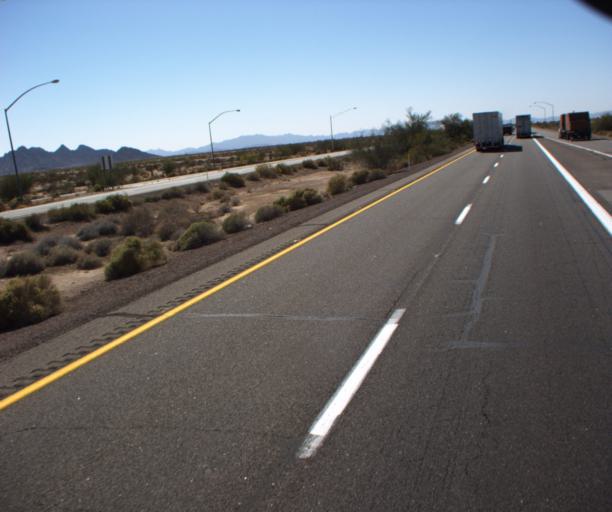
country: US
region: Arizona
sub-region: Yuma County
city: Wellton
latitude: 32.6932
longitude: -113.9563
